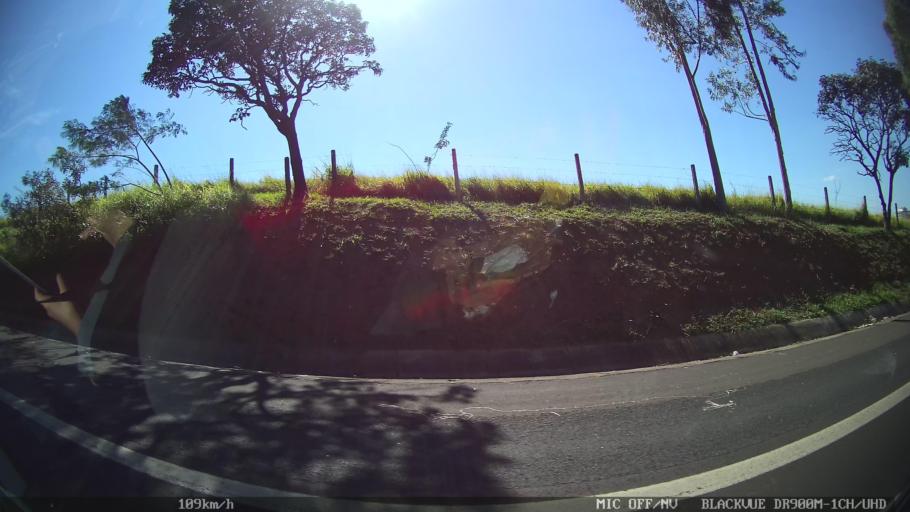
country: BR
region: Sao Paulo
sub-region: Franca
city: Franca
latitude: -20.5546
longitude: -47.4245
